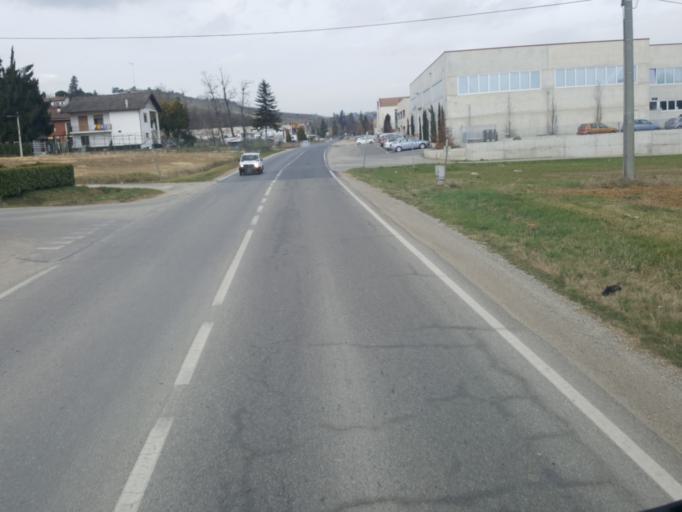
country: IT
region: Piedmont
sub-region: Provincia di Asti
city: Canelli
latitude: 44.7345
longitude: 8.2923
